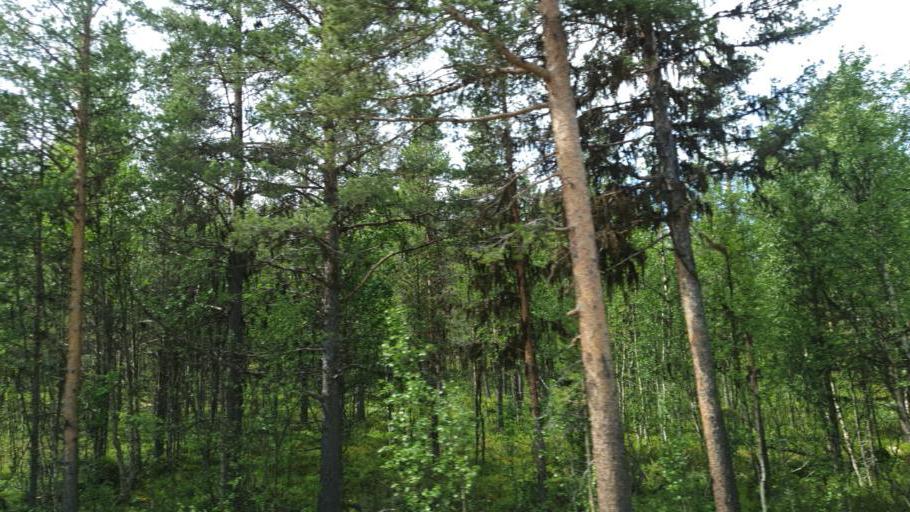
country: NO
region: Oppland
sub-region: Vaga
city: Vagamo
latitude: 61.7038
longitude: 9.0583
